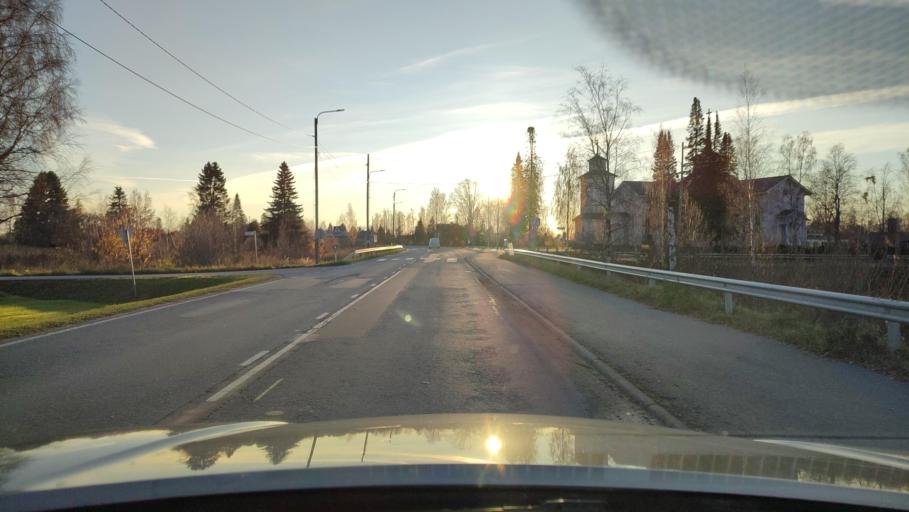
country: FI
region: Ostrobothnia
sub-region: Sydosterbotten
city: Naerpes
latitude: 62.6097
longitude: 21.4669
